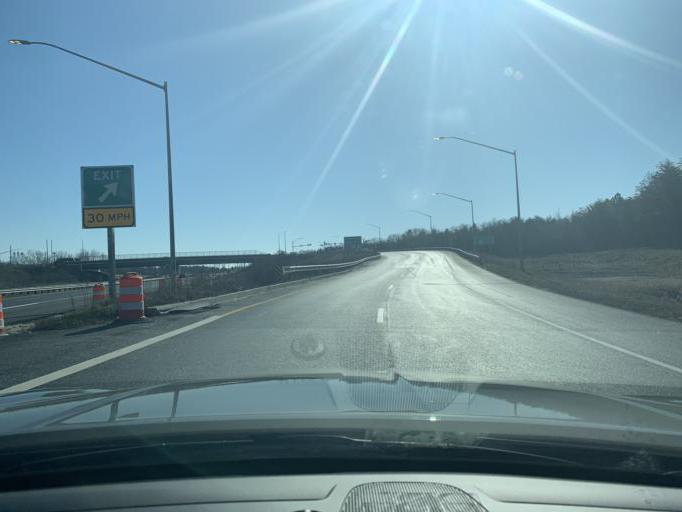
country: US
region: Maryland
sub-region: Prince George's County
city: Brandywine
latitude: 38.7071
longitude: -76.8779
